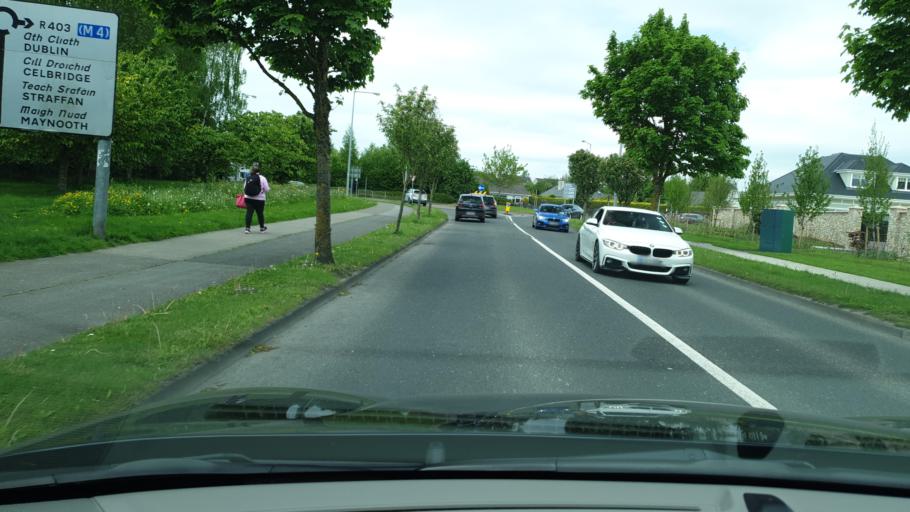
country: IE
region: Leinster
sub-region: Kildare
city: Clane
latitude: 53.2945
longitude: -6.6810
